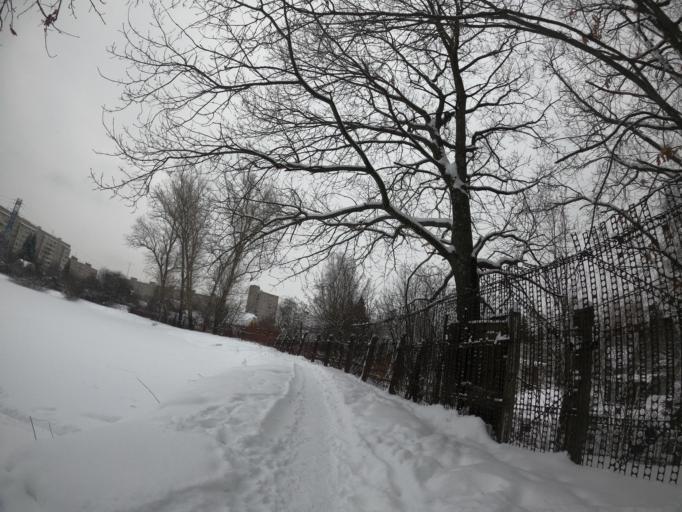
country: RU
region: Moskovskaya
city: Vostryakovo
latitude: 55.4148
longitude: 37.8271
